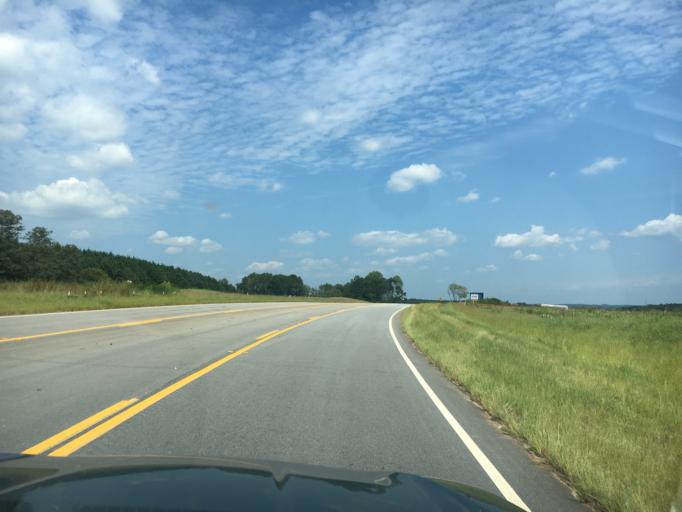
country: US
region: South Carolina
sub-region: Spartanburg County
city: Roebuck
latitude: 34.8717
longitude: -82.0322
